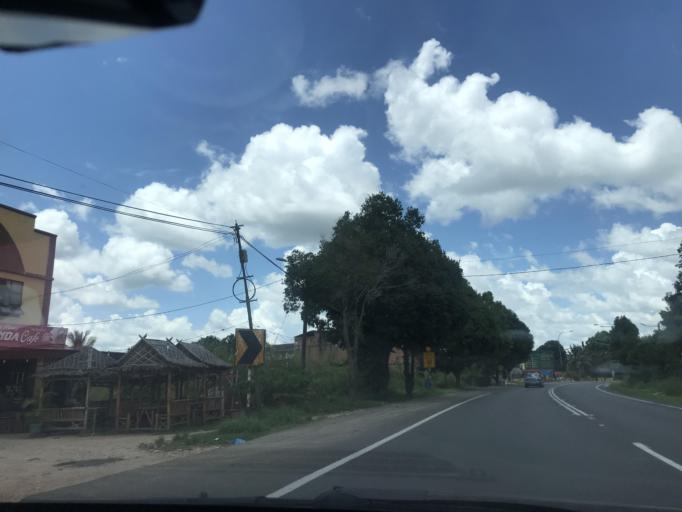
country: MY
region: Kelantan
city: Tumpat
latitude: 6.2119
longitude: 102.1107
